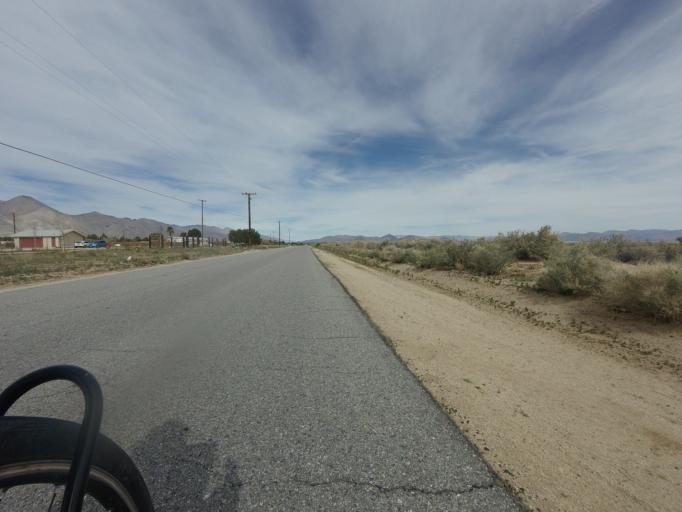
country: US
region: California
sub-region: Kern County
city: Inyokern
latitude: 35.7527
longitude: -117.8437
